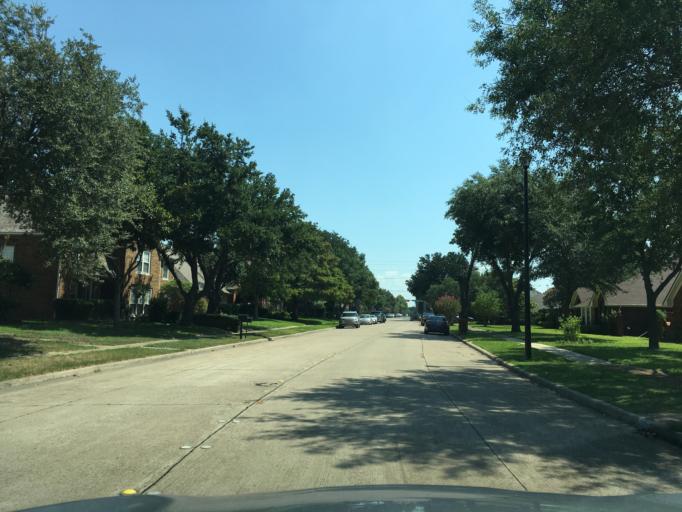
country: US
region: Texas
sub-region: Dallas County
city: Garland
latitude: 32.9388
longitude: -96.6672
